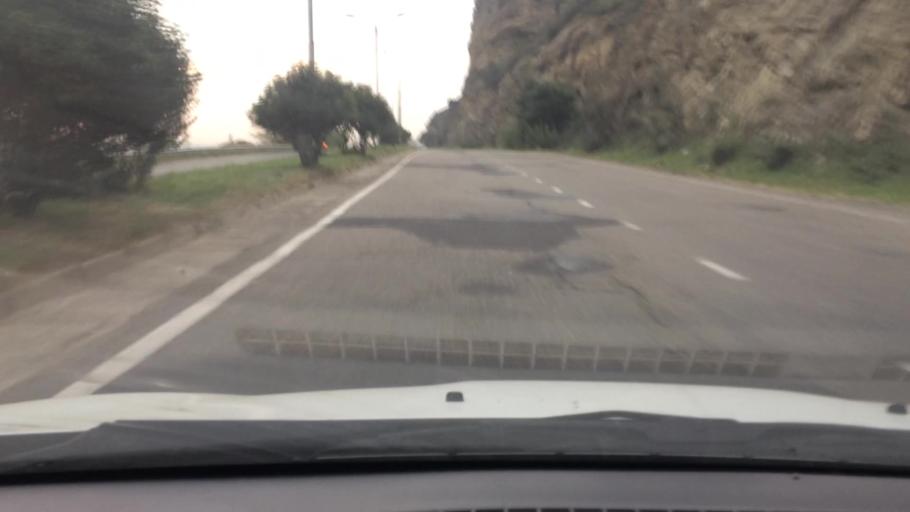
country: GE
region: T'bilisi
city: Tbilisi
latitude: 41.6546
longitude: 44.8978
